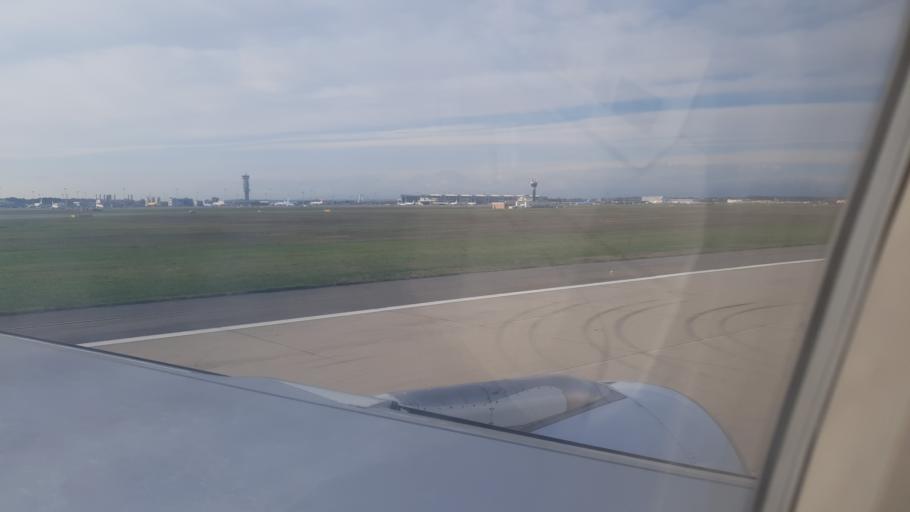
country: IT
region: Lombardy
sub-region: Provincia di Varese
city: Ferno
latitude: 45.6172
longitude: 8.7371
